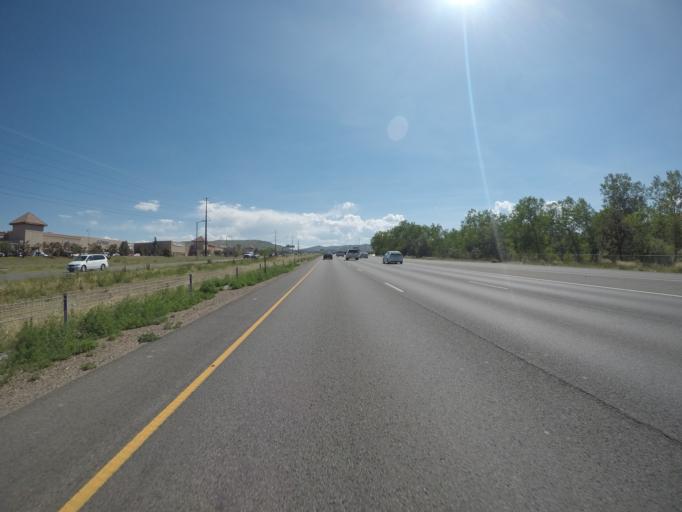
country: US
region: Colorado
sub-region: Jefferson County
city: West Pleasant View
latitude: 39.7378
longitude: -105.1623
